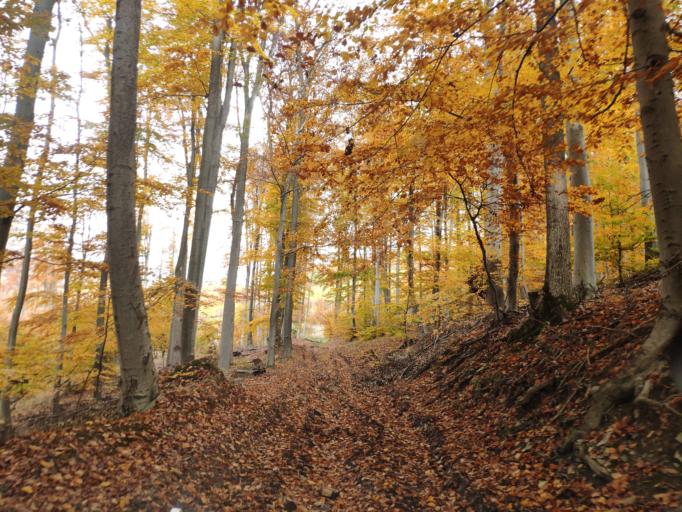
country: SK
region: Kosicky
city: Medzev
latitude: 48.7354
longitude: 20.9873
